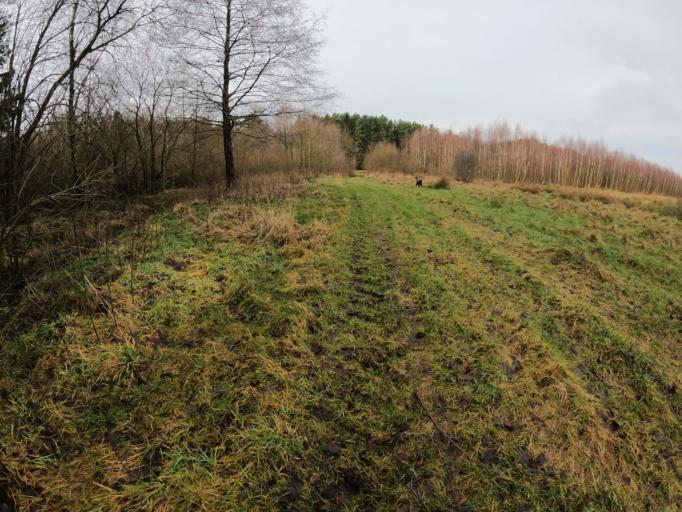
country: PL
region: West Pomeranian Voivodeship
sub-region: Powiat slawienski
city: Darlowo
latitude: 54.4217
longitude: 16.4954
